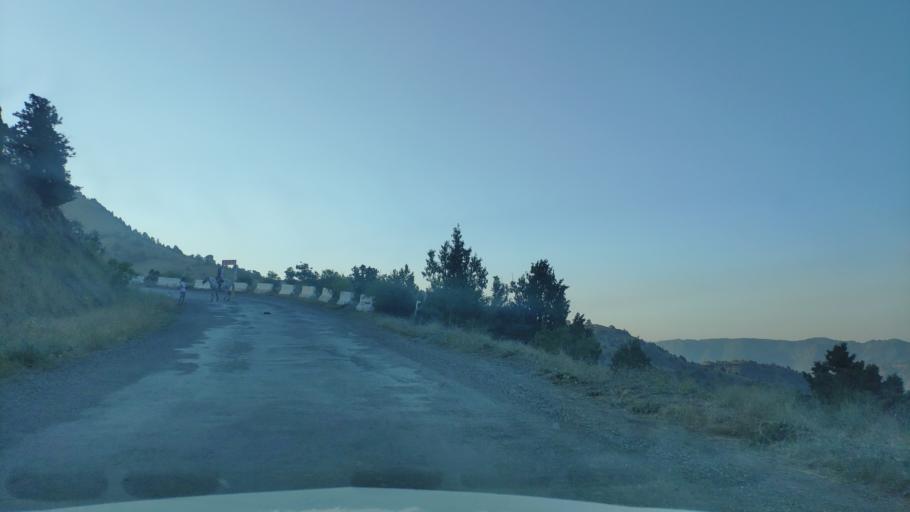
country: TJ
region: Viloyati Sughd
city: Ayni
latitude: 39.6388
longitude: 68.4763
